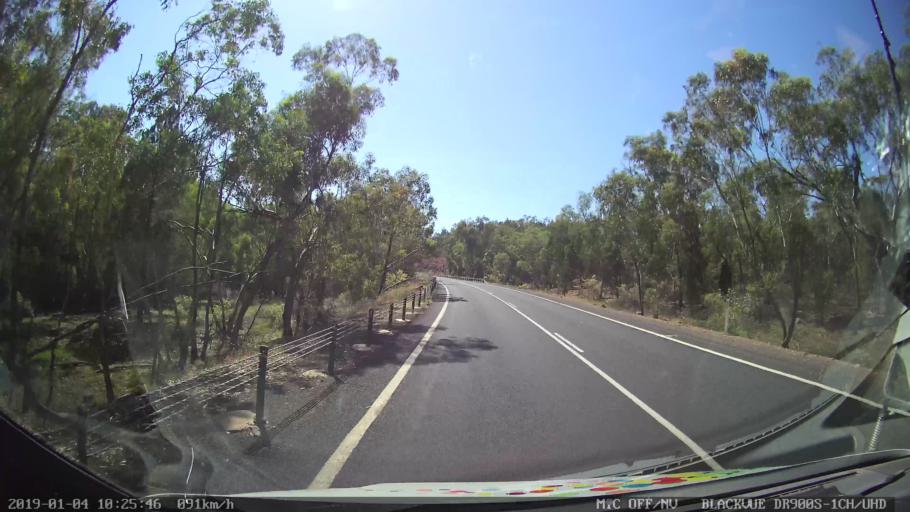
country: AU
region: New South Wales
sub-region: Cabonne
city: Canowindra
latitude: -33.3718
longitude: 148.5742
